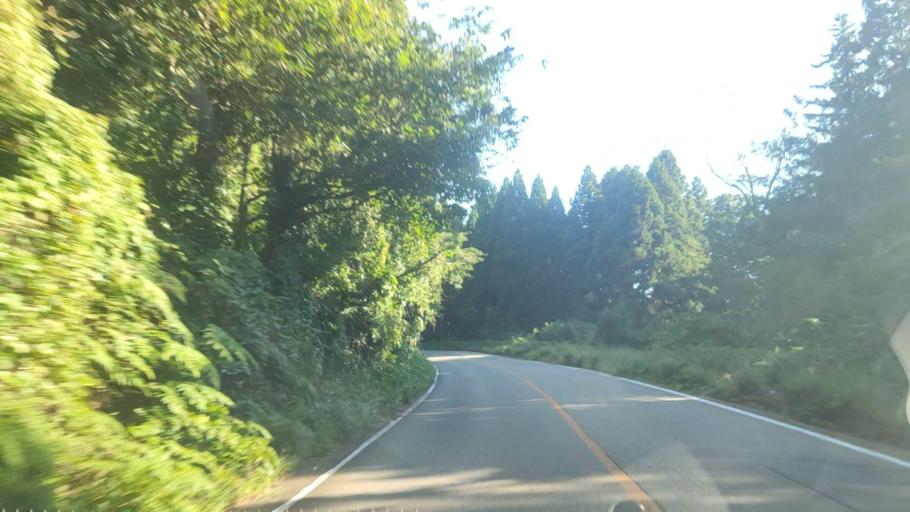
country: JP
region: Ishikawa
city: Nanao
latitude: 37.1050
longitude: 136.9473
